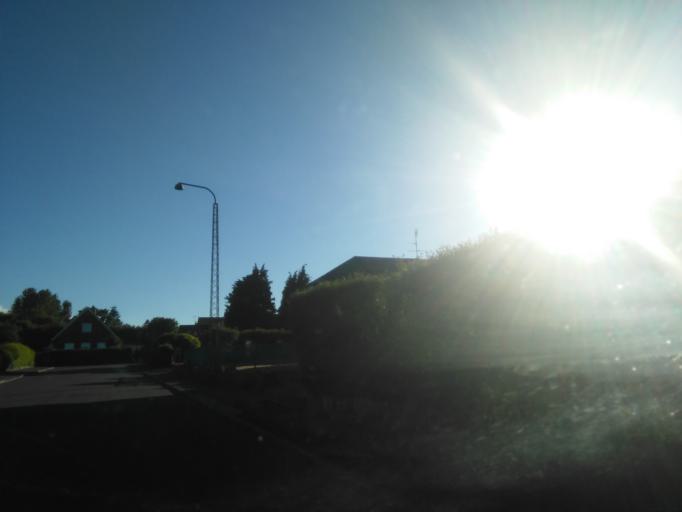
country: DK
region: Capital Region
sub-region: Bornholm Kommune
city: Ronne
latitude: 55.2708
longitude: 14.8026
